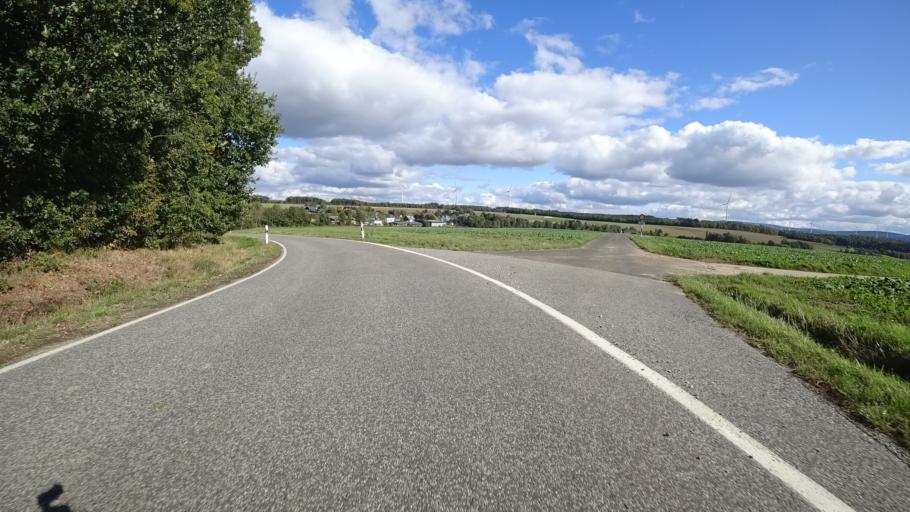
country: DE
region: Rheinland-Pfalz
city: Klosterkumbd
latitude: 50.0257
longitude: 7.5233
